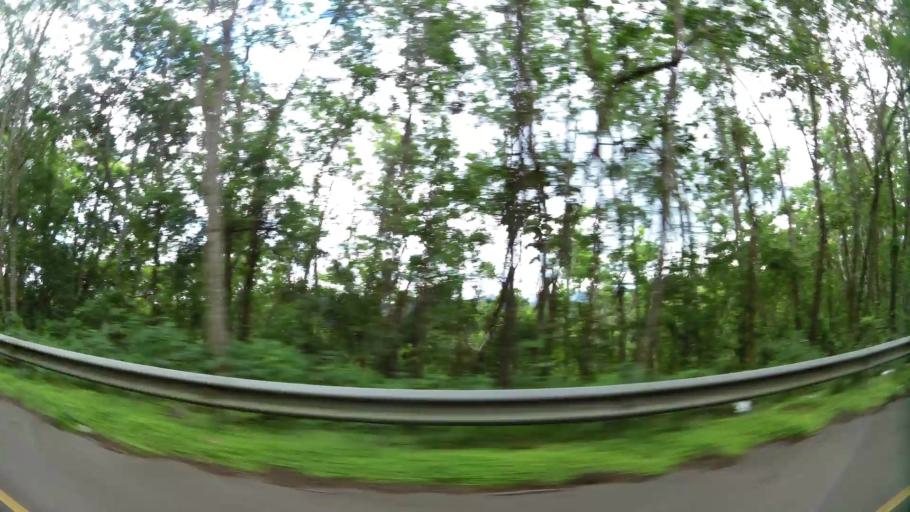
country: DO
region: Monsenor Nouel
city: Sabana del Puerto
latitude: 19.0853
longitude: -70.4408
